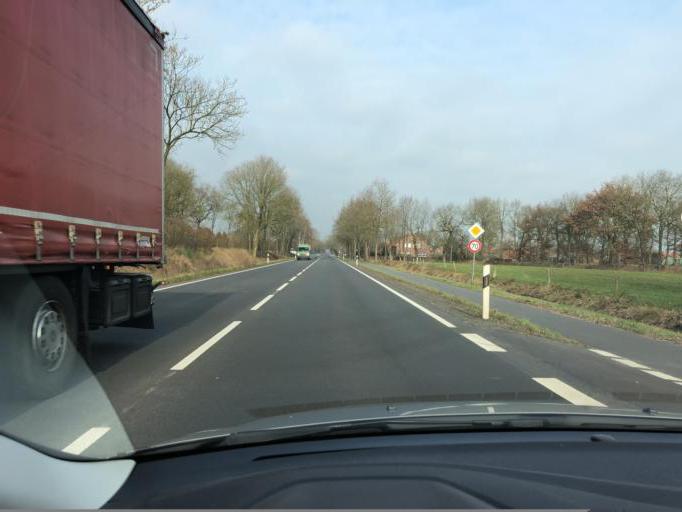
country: DE
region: Lower Saxony
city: Hesel
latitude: 53.3477
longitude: 7.6040
